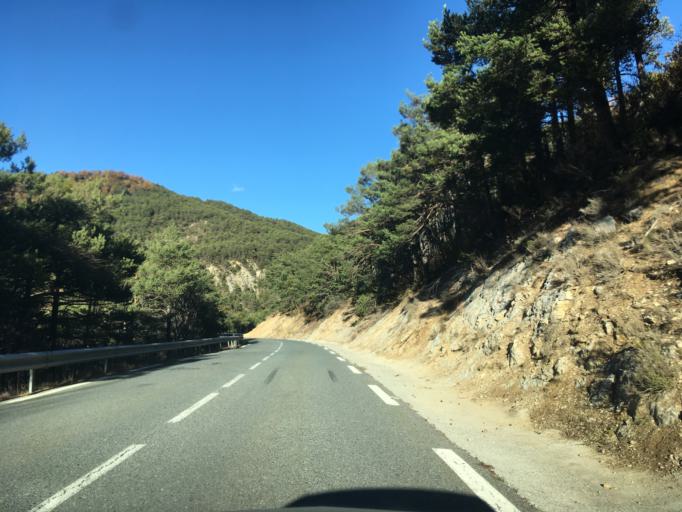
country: FR
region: Provence-Alpes-Cote d'Azur
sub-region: Departement des Alpes-de-Haute-Provence
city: Castellane
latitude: 43.7345
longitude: 6.5019
